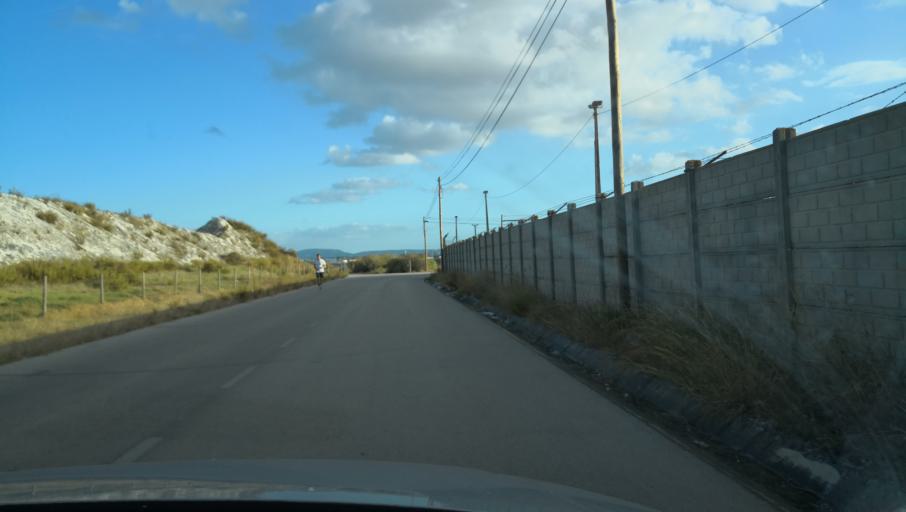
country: PT
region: Setubal
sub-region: Moita
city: Alhos Vedros
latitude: 38.6724
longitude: -9.0451
